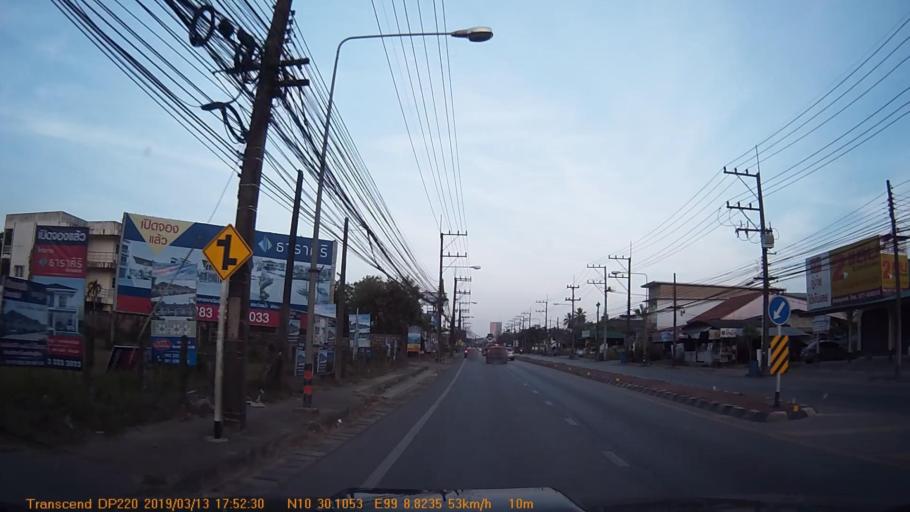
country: TH
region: Chumphon
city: Chumphon
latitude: 10.5018
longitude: 99.1473
